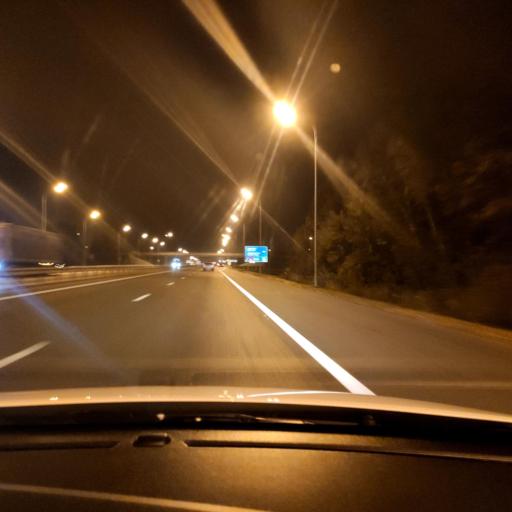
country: RU
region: Tatarstan
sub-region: Gorod Kazan'
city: Kazan
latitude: 55.9107
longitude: 49.0677
